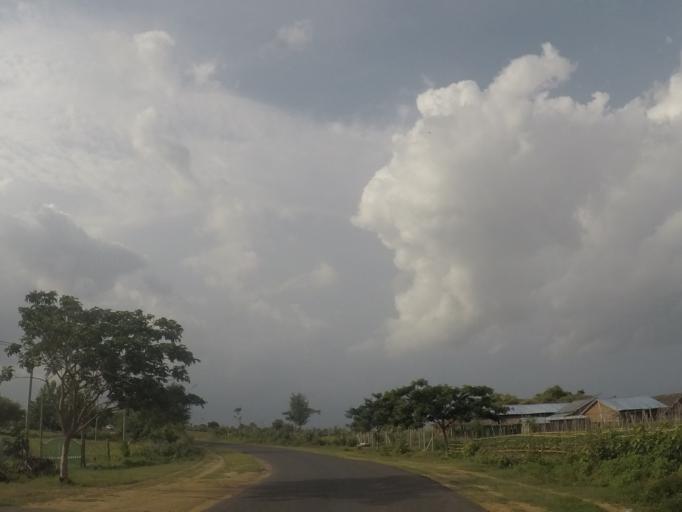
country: MM
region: Mandalay
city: Meiktila
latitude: 20.5163
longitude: 95.7097
